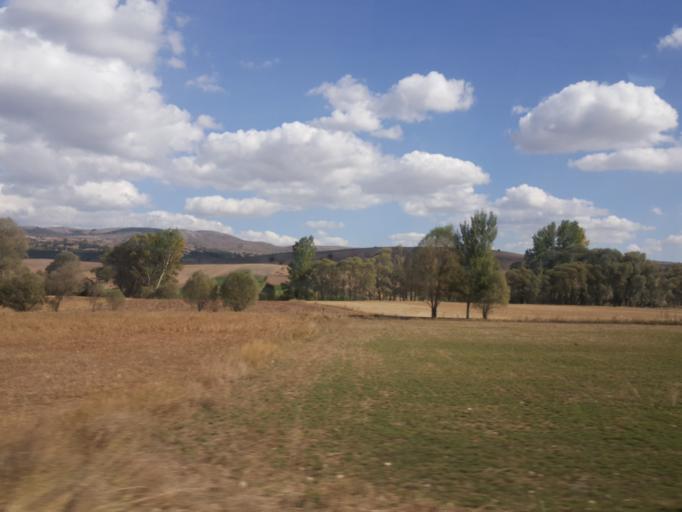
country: TR
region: Tokat
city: Camlibel
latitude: 40.1911
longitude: 36.4570
